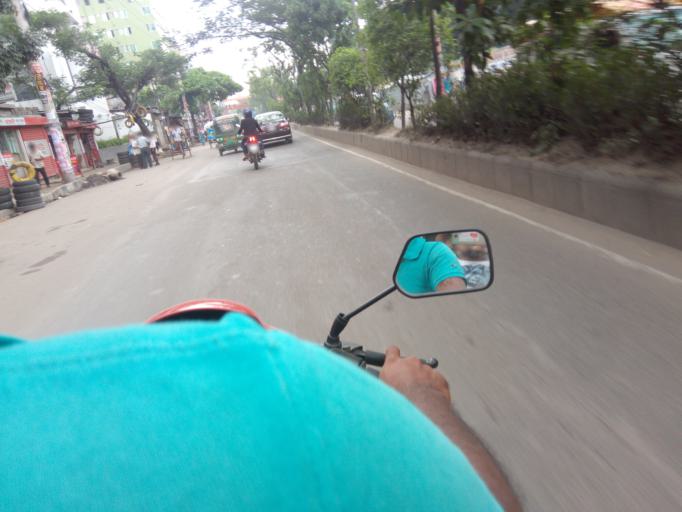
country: BD
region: Dhaka
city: Paltan
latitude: 23.7343
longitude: 90.4286
